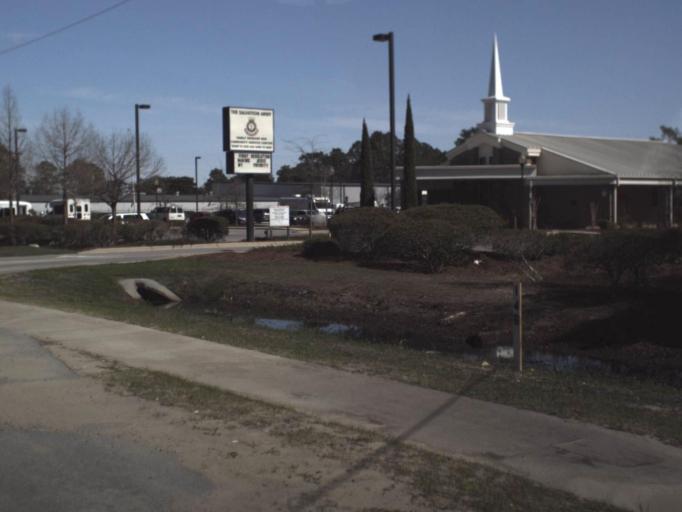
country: US
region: Florida
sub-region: Bay County
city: Hiland Park
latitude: 30.2175
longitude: -85.6493
